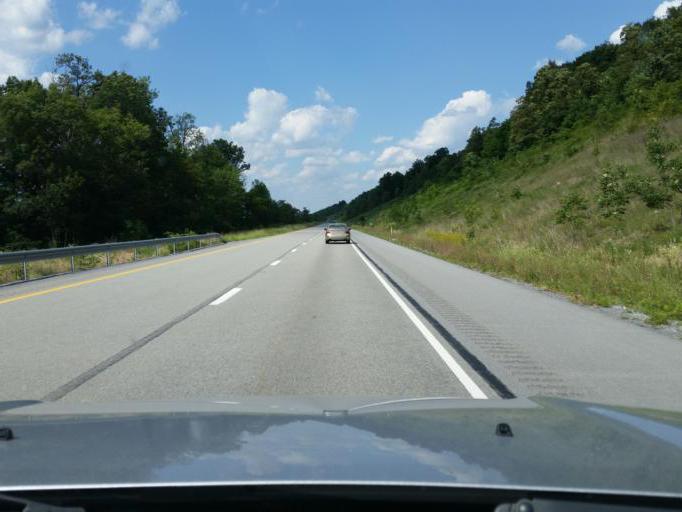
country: US
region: Pennsylvania
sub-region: Blair County
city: Claysburg
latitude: 40.2864
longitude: -78.4469
